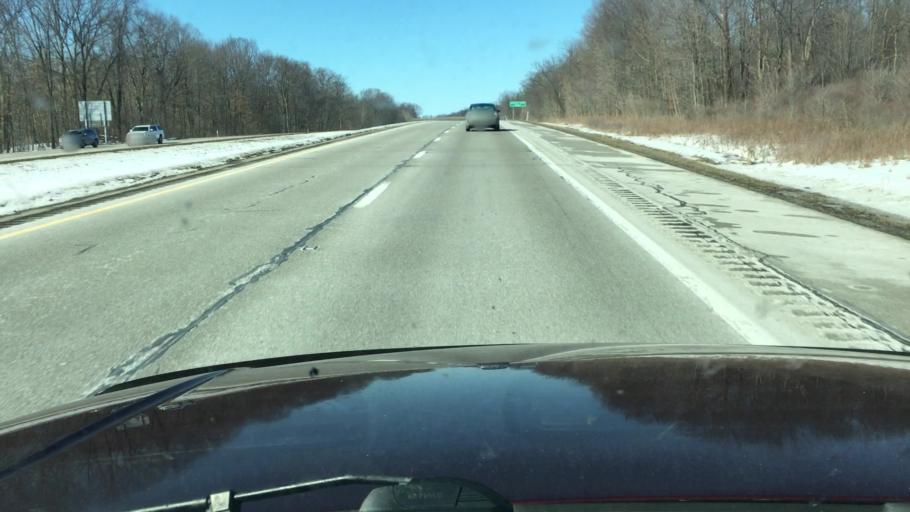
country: US
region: Pennsylvania
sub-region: Crawford County
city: Cochranton
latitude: 41.4842
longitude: -80.1665
